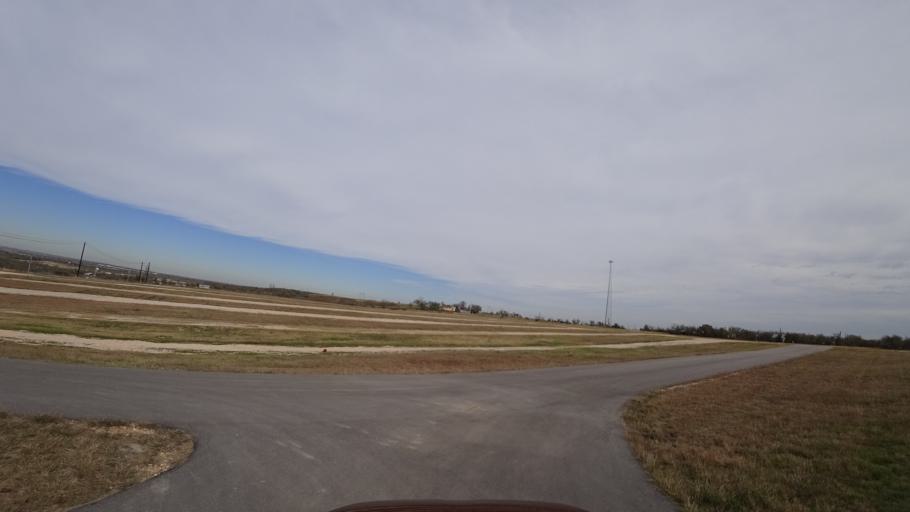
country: US
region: Texas
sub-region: Travis County
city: Garfield
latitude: 30.1387
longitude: -97.6227
